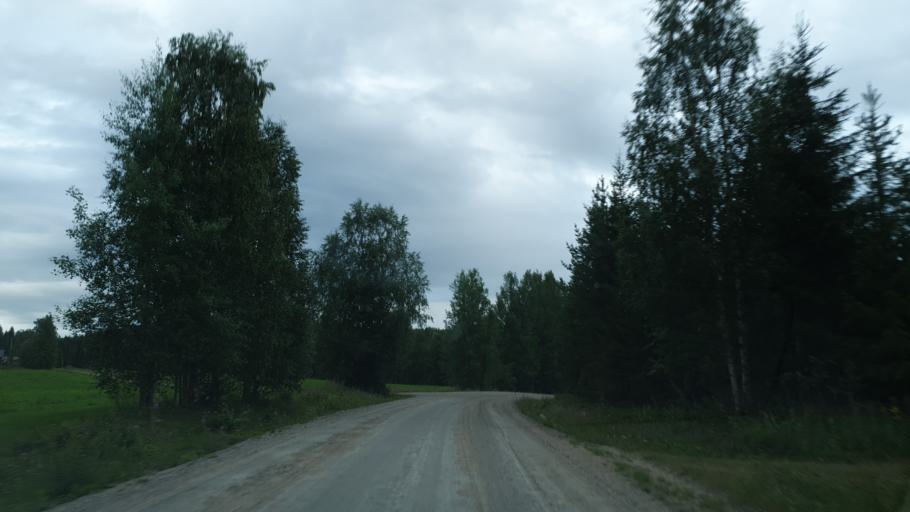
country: FI
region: Kainuu
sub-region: Kehys-Kainuu
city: Kuhmo
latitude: 64.2048
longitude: 29.3731
